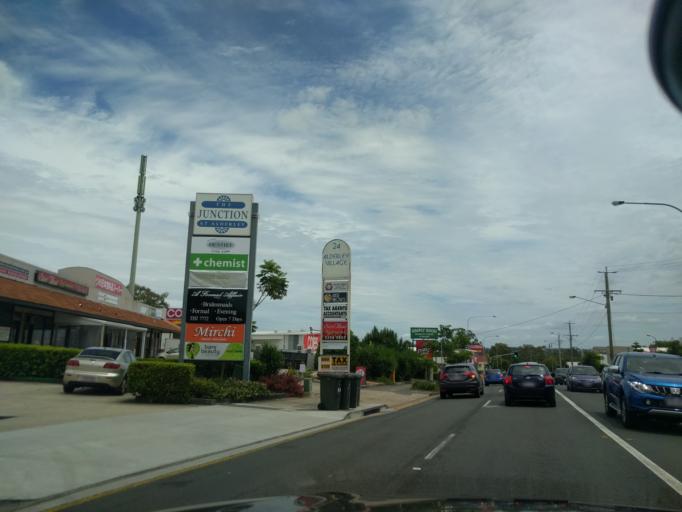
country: AU
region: Queensland
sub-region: Brisbane
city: Grange
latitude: -27.4249
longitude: 153.0008
